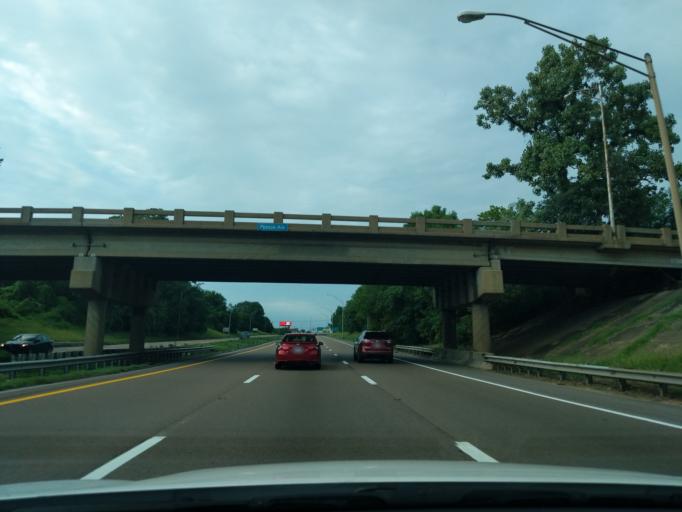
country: US
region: Tennessee
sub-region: Shelby County
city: New South Memphis
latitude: 35.1017
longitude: -90.0761
